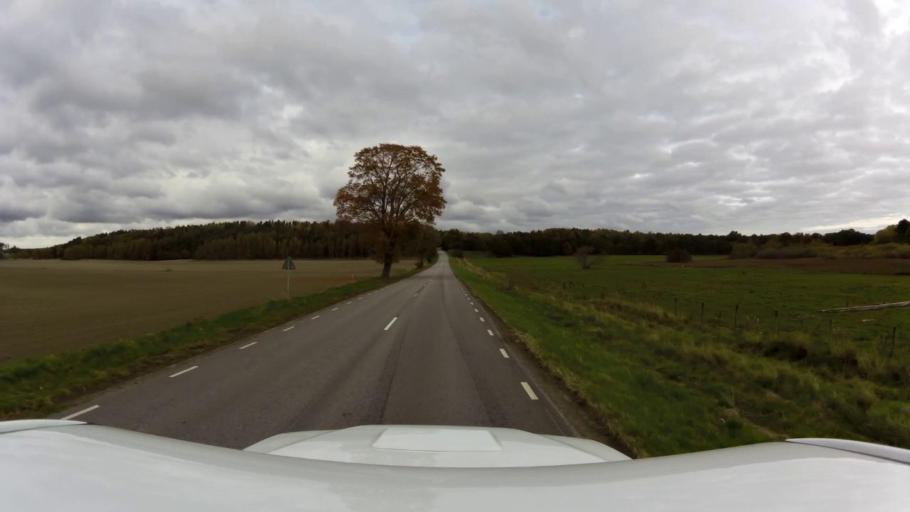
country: SE
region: OEstergoetland
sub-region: Linkopings Kommun
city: Berg
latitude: 58.5037
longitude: 15.5391
